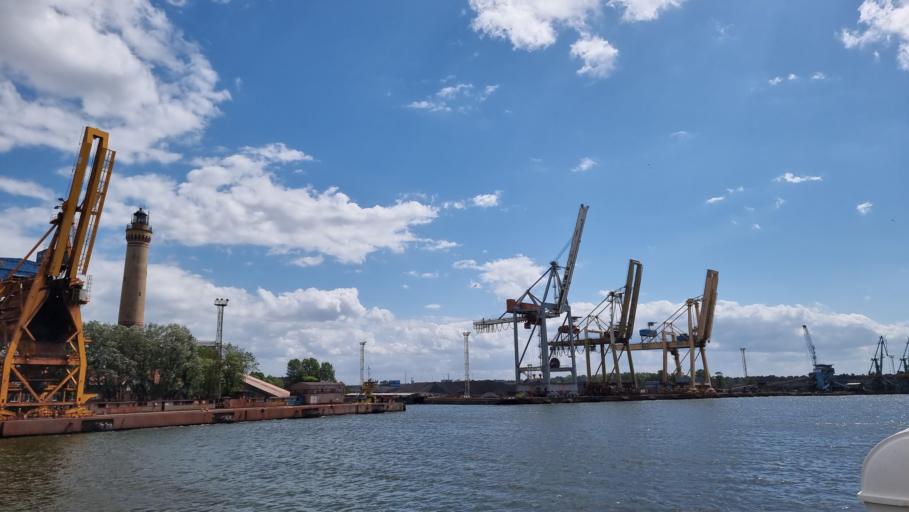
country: PL
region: West Pomeranian Voivodeship
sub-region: Swinoujscie
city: Swinoujscie
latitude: 53.9173
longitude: 14.2815
